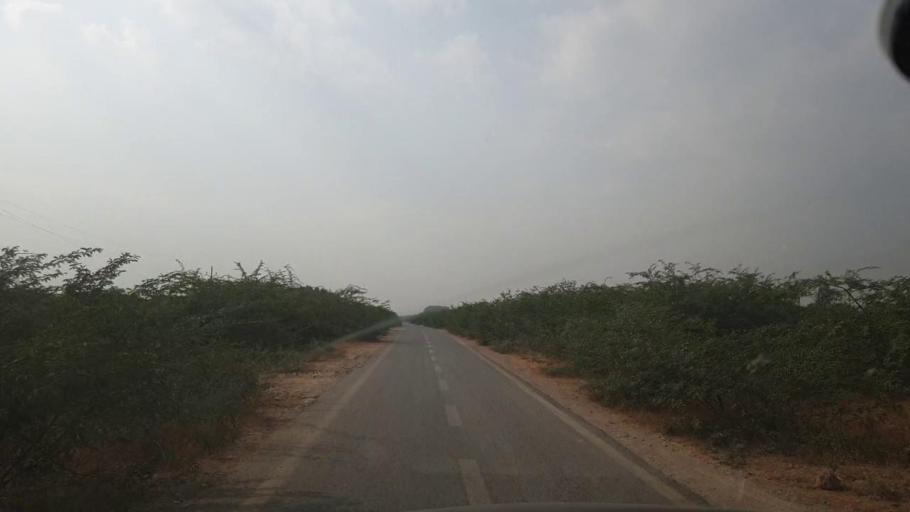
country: PK
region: Sindh
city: Malir Cantonment
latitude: 24.9470
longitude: 67.2934
